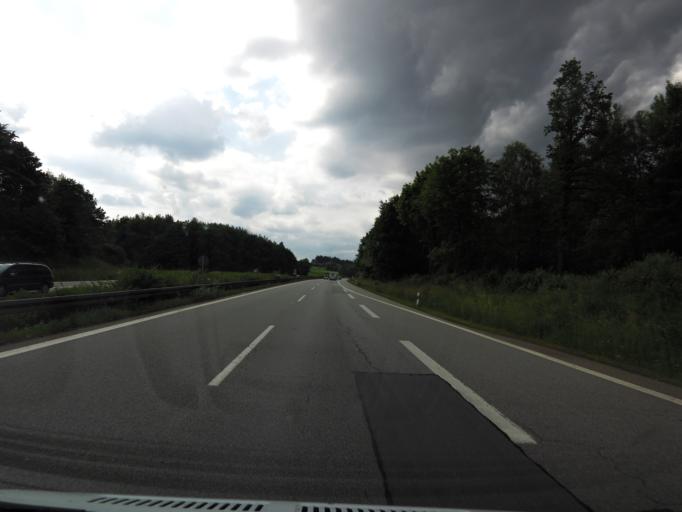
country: DE
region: Bavaria
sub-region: Lower Bavaria
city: Aussernzell
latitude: 48.6874
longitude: 13.2077
